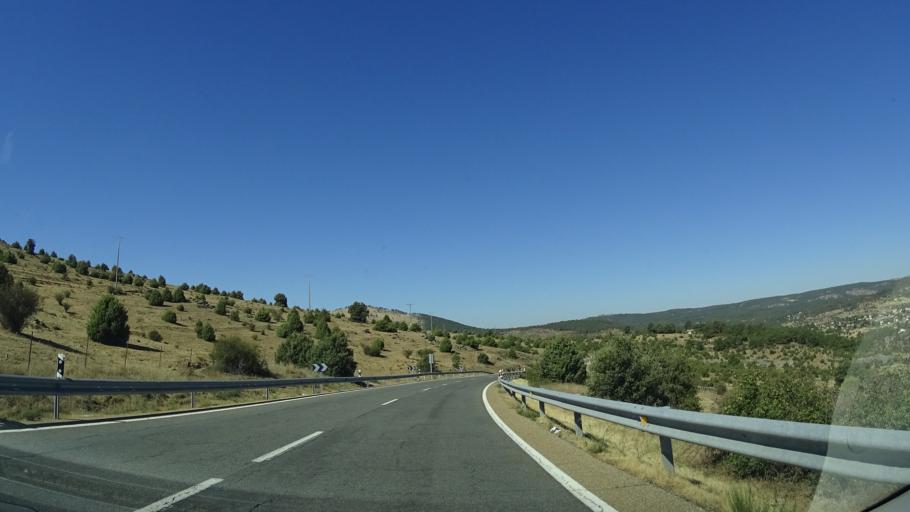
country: ES
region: Madrid
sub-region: Provincia de Madrid
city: Santa Maria de la Alameda
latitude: 40.5593
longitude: -4.2481
